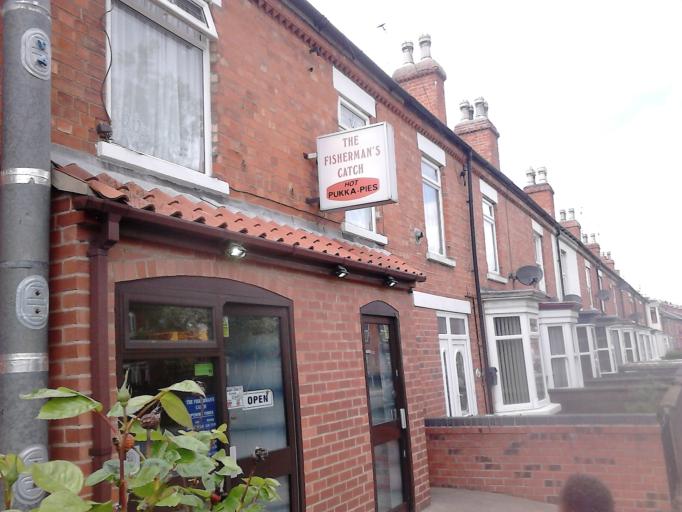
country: GB
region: England
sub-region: Nottinghamshire
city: Newark on Trent
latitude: 53.0698
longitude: -0.8052
